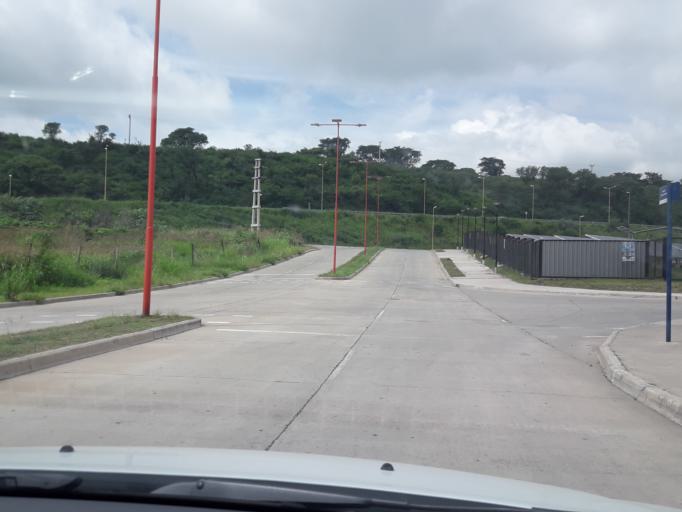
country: AR
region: Jujuy
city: San Salvador de Jujuy
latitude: -24.1844
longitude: -65.3297
